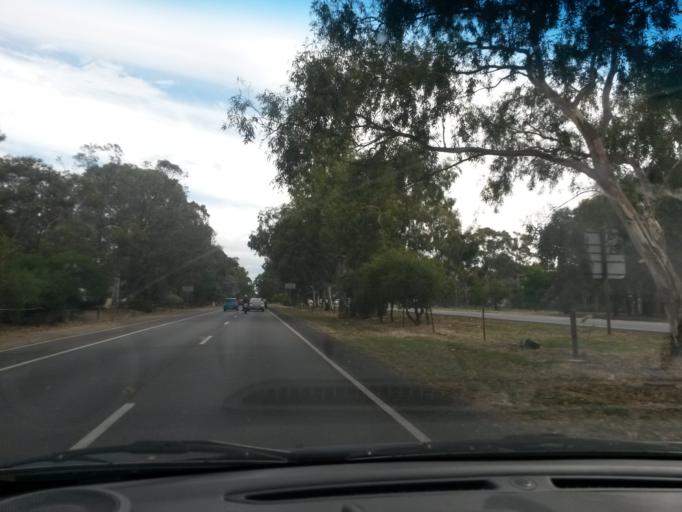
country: AU
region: South Australia
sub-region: Salisbury
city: Salisbury
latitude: -34.7848
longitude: 138.6530
